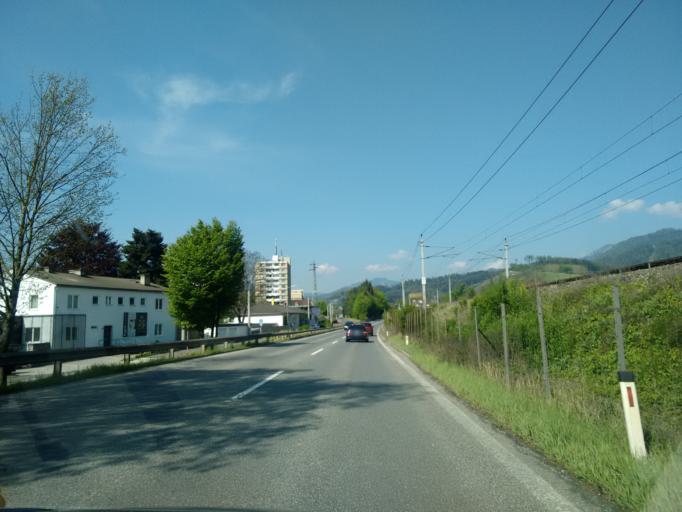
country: AT
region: Styria
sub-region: Politischer Bezirk Bruck-Muerzzuschlag
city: Kapfenberg
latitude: 47.4511
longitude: 15.3173
